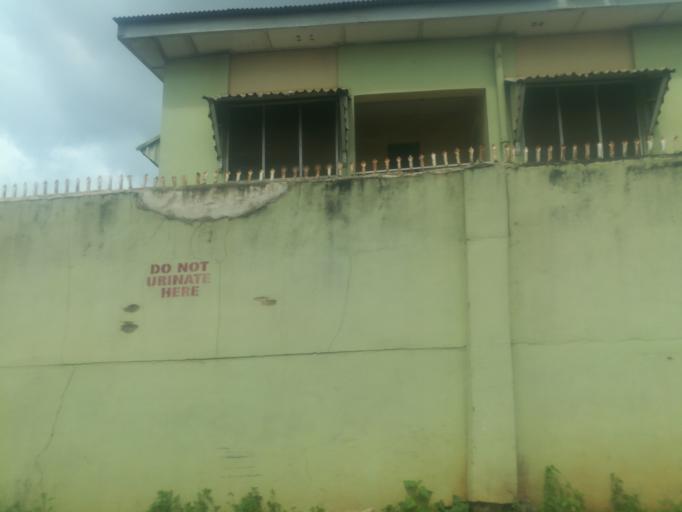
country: NG
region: Oyo
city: Ibadan
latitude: 7.4056
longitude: 3.9302
